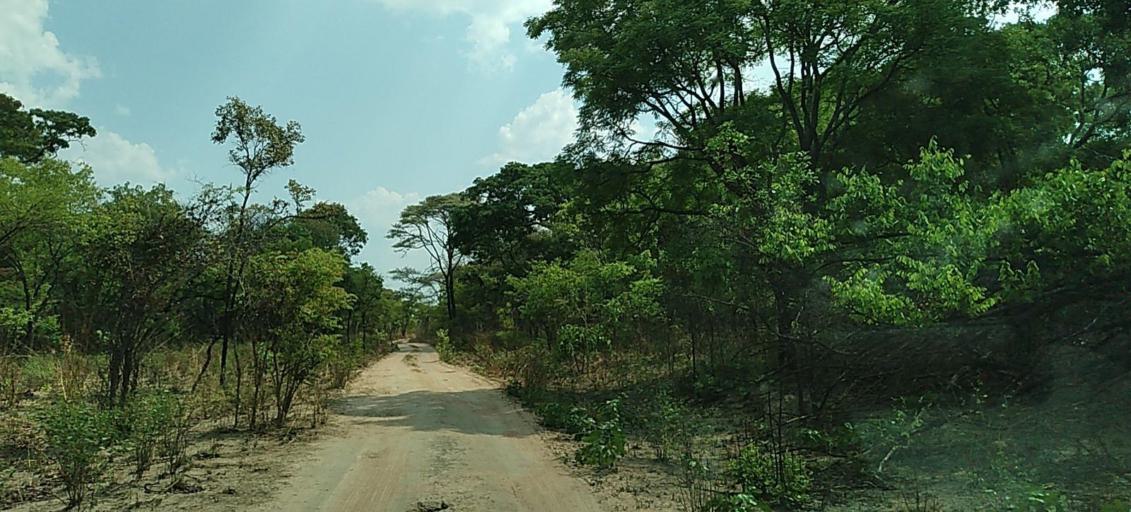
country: ZM
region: Copperbelt
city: Mpongwe
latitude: -13.8678
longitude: 27.9248
